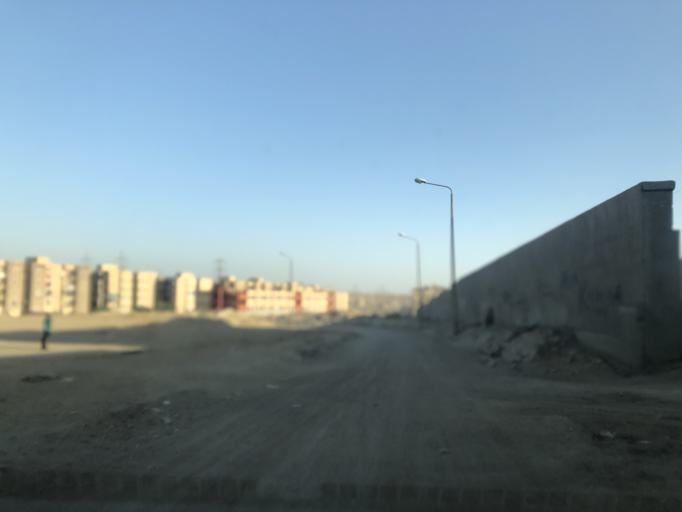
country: EG
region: Al Jizah
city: Al Jizah
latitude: 29.9880
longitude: 31.1072
